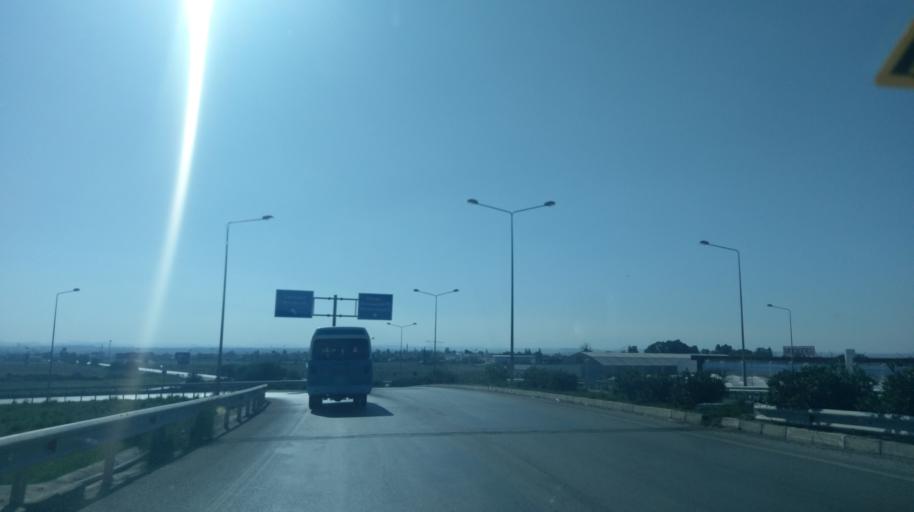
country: CY
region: Lefkosia
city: Geri
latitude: 35.2187
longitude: 33.4978
